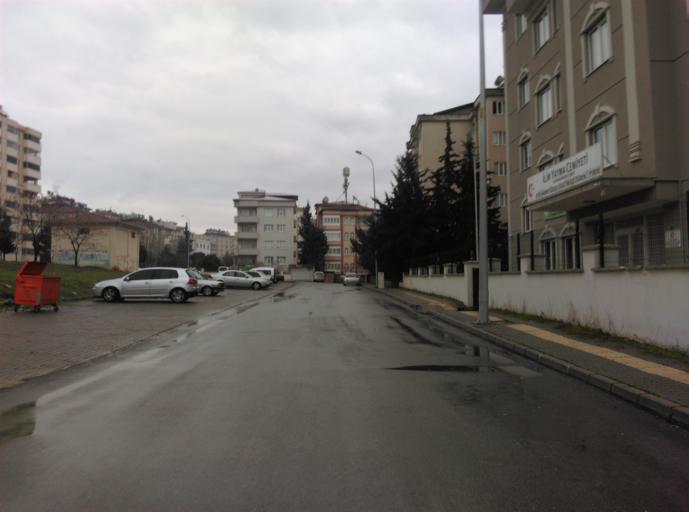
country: TR
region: Kahramanmaras
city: Kahramanmaras
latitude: 37.5856
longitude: 36.8928
